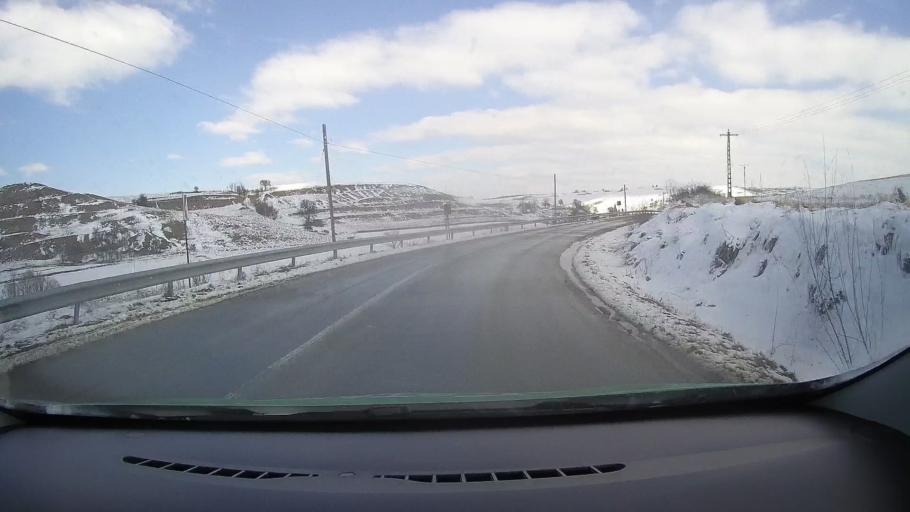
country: RO
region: Sibiu
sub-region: Comuna Barghis
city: Barghis
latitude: 45.9809
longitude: 24.5260
